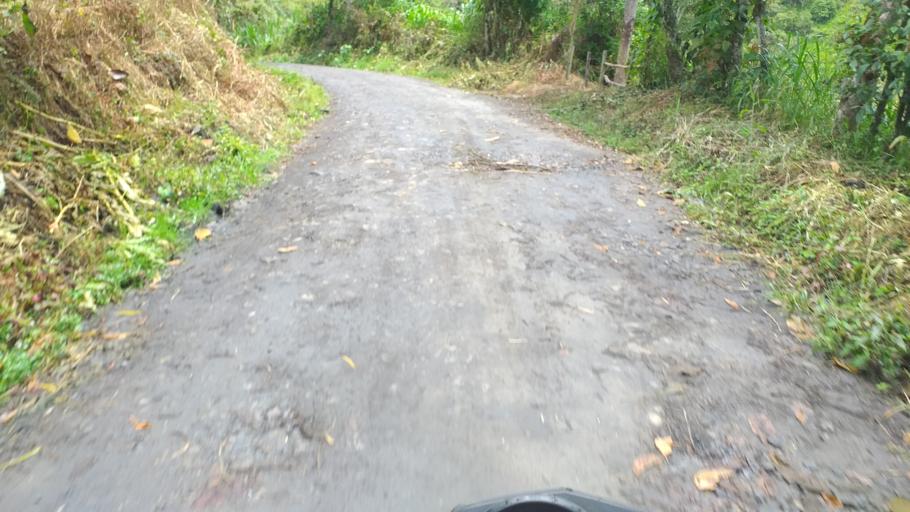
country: CO
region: Cundinamarca
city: Tenza
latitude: 5.1093
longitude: -73.4512
